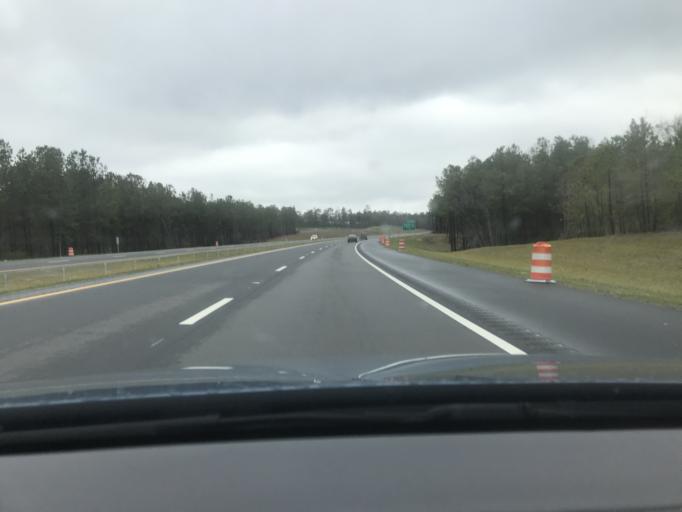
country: US
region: North Carolina
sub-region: Cumberland County
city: Fort Bragg
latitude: 35.0895
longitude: -79.0257
